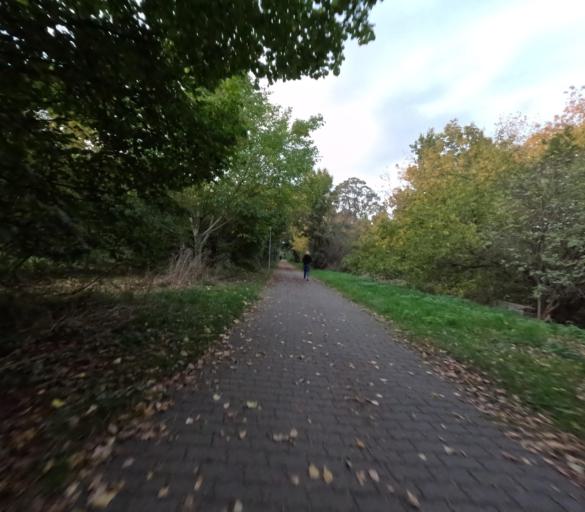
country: DE
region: Saxony
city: Naunhof
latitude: 51.2821
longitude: 12.5837
